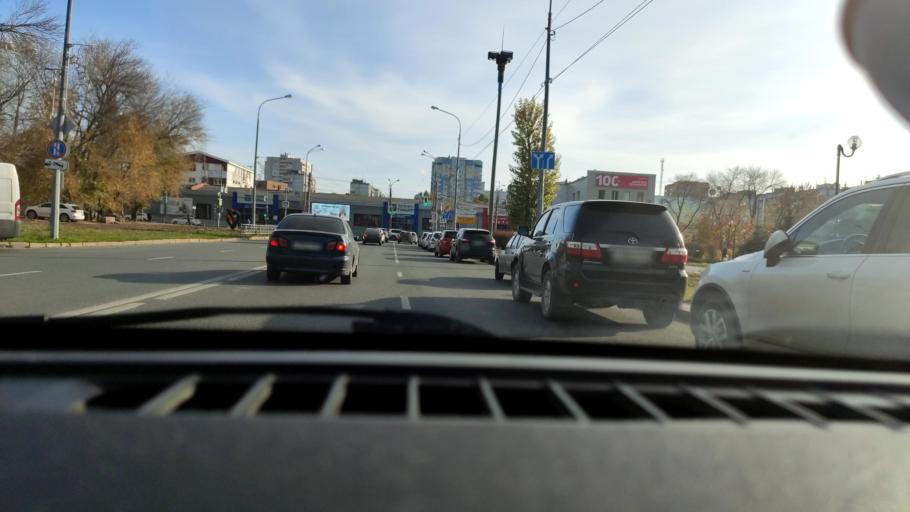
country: RU
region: Samara
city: Samara
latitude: 53.2049
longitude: 50.1394
